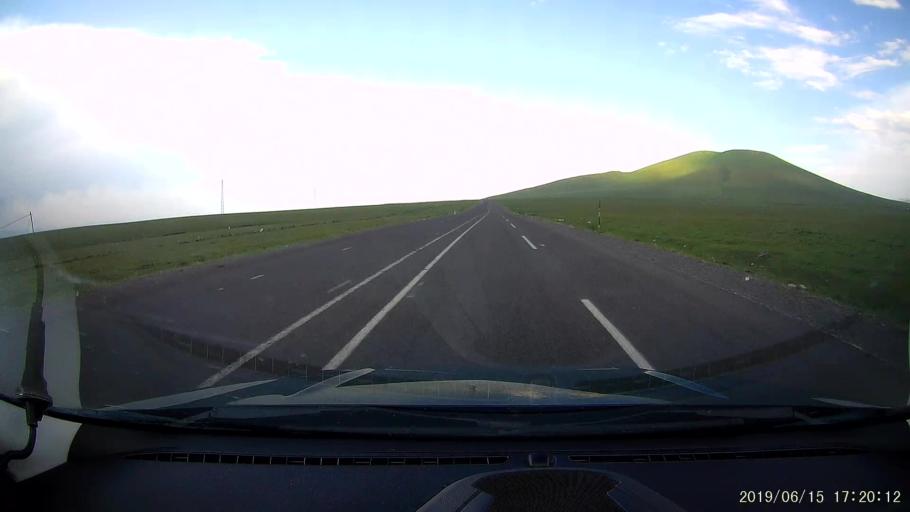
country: TR
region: Kars
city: Kars
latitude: 40.6161
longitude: 43.2957
